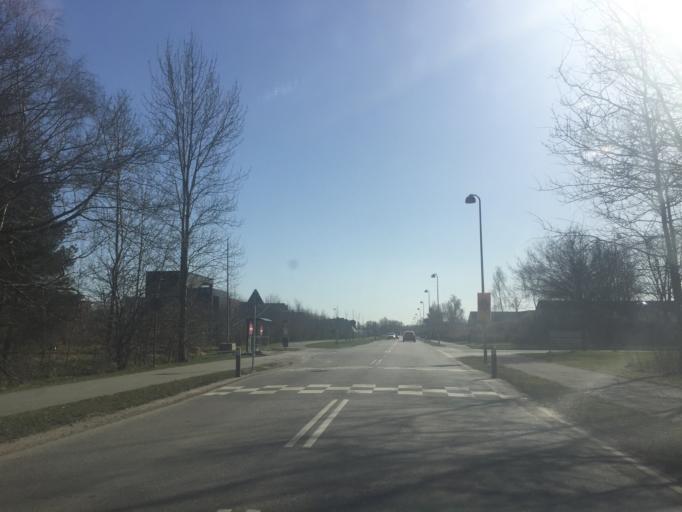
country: DK
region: Capital Region
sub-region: Glostrup Kommune
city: Glostrup
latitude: 55.6857
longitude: 12.4208
